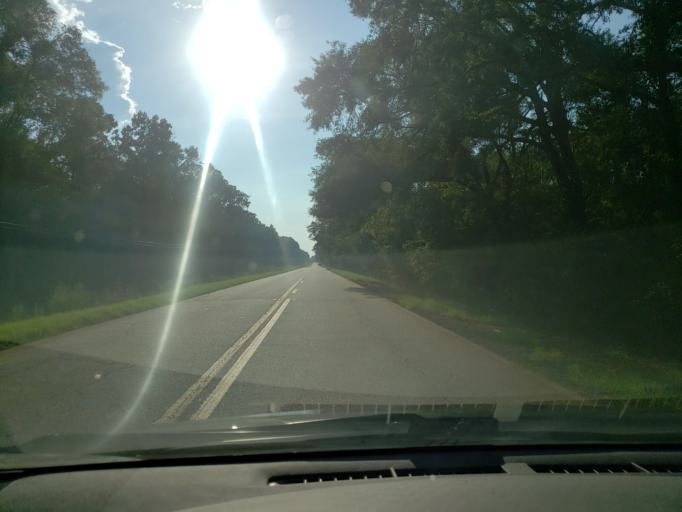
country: US
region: Georgia
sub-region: Dougherty County
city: Albany
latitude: 31.5743
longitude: -84.3420
